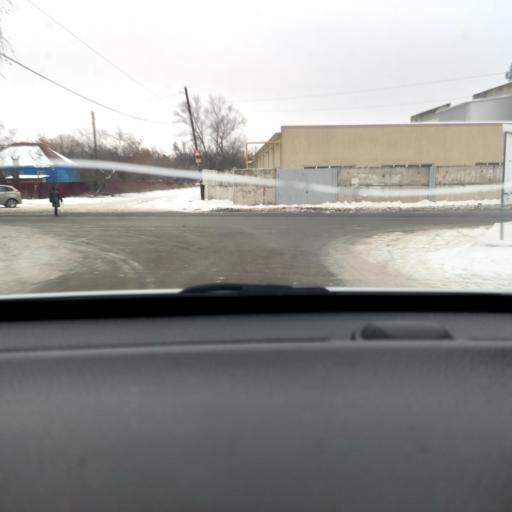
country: RU
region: Voronezj
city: Somovo
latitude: 51.7413
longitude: 39.3566
